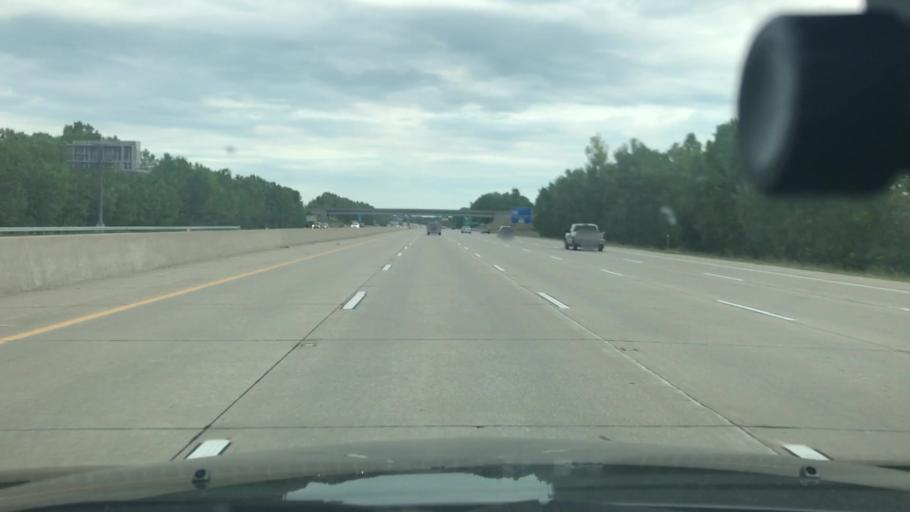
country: US
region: Missouri
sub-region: Saint Charles County
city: Saint Charles
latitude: 38.7223
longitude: -90.5123
